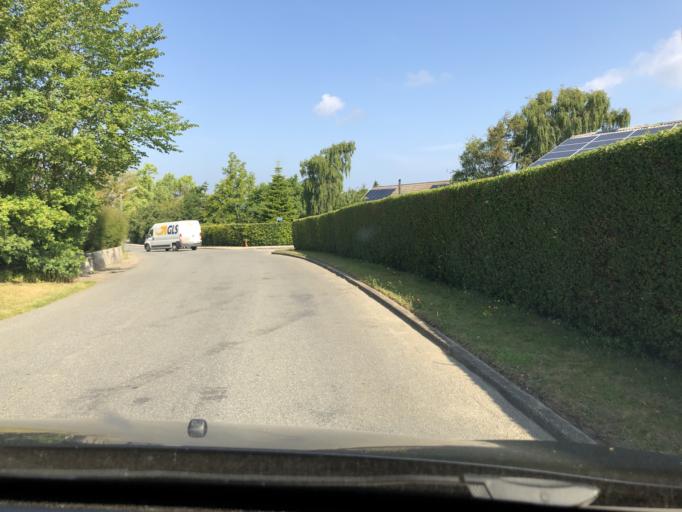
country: DK
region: South Denmark
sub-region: Faaborg-Midtfyn Kommune
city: Faaborg
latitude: 54.9408
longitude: 10.2519
